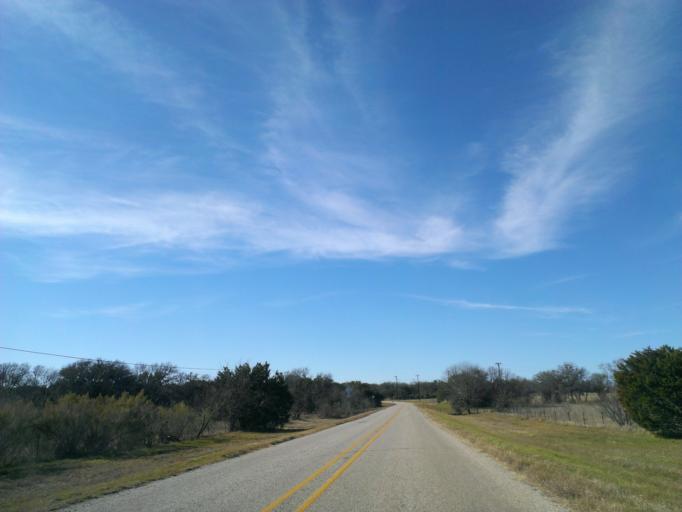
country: US
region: Texas
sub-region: Burnet County
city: Marble Falls
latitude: 30.5468
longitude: -98.2222
